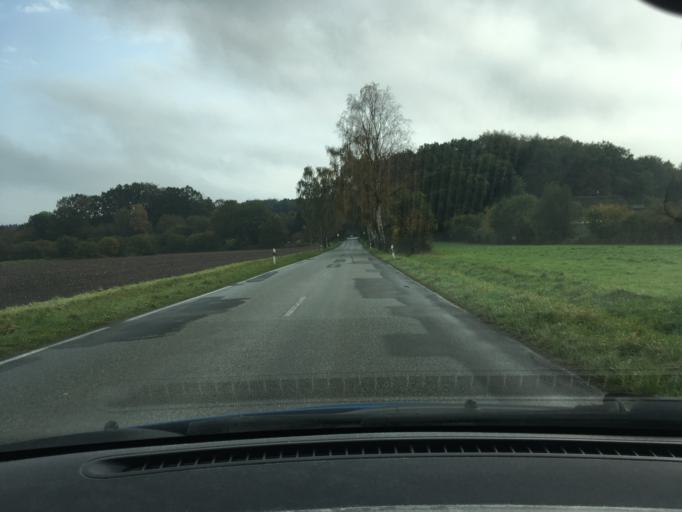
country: DE
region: Schleswig-Holstein
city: Blunk
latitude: 54.0197
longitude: 10.3197
